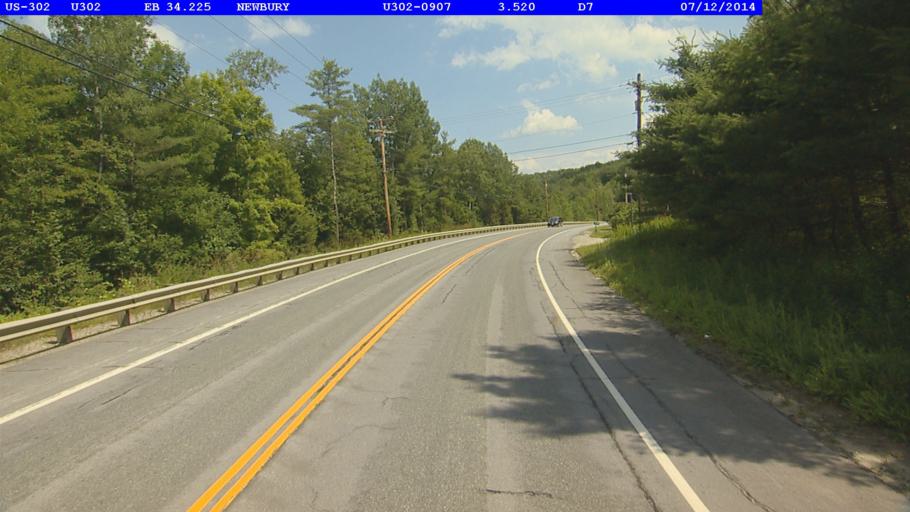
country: US
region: New Hampshire
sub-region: Grafton County
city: Woodsville
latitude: 44.1501
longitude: -72.0656
